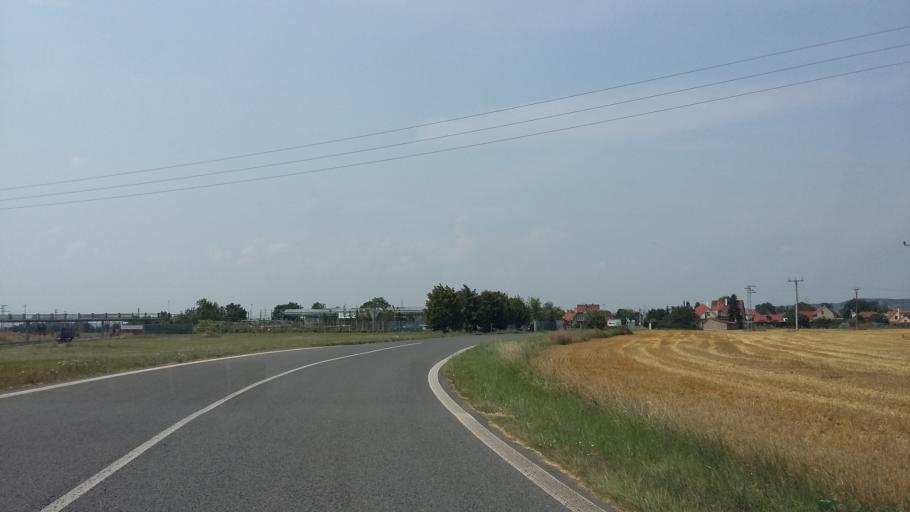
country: CZ
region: Central Bohemia
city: Luzec nad Vltavou
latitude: 50.3369
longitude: 14.3703
